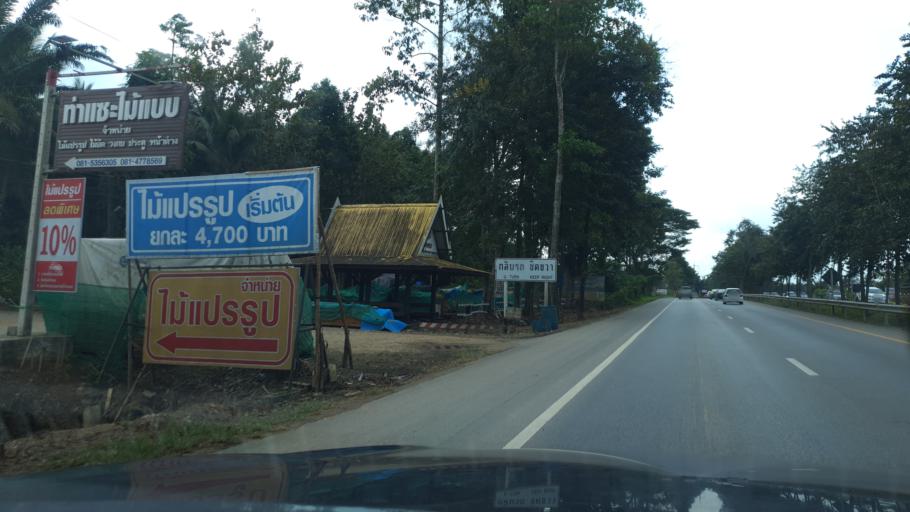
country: TH
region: Chumphon
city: Tha Sae
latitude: 10.6389
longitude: 99.1841
